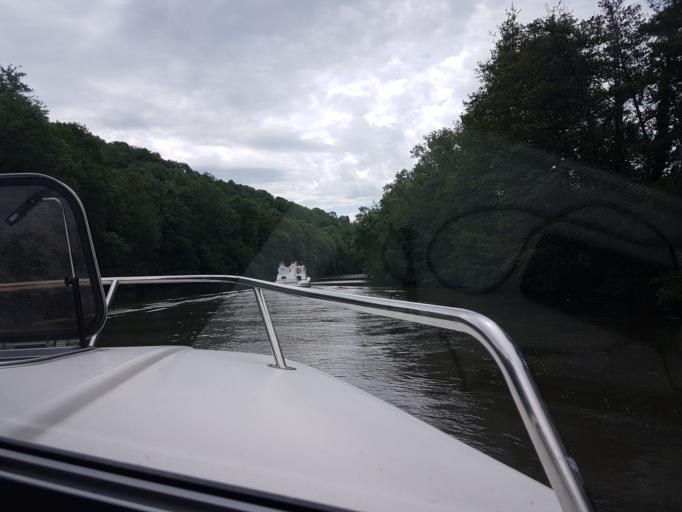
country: FR
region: Bourgogne
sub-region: Departement de la Nievre
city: Clamecy
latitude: 47.4687
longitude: 3.5282
